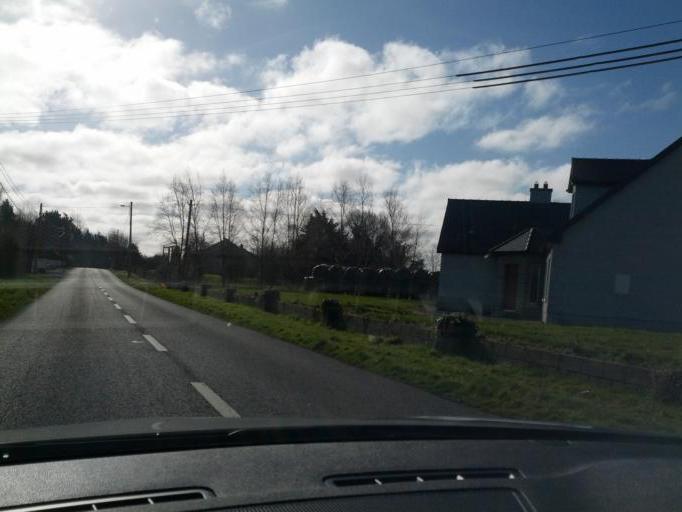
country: IE
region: Connaught
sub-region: County Galway
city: Ballinasloe
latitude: 53.3440
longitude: -8.2462
